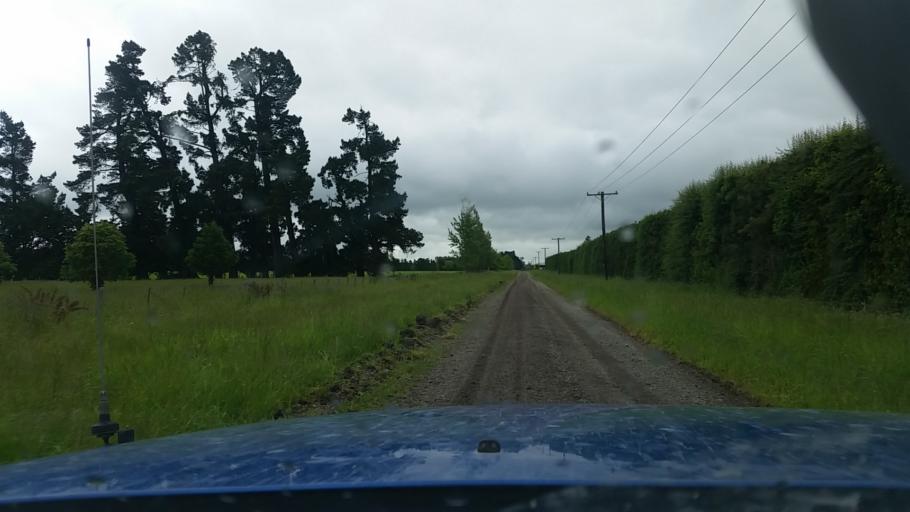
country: NZ
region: Canterbury
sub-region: Ashburton District
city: Methven
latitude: -43.7018
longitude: 171.4322
